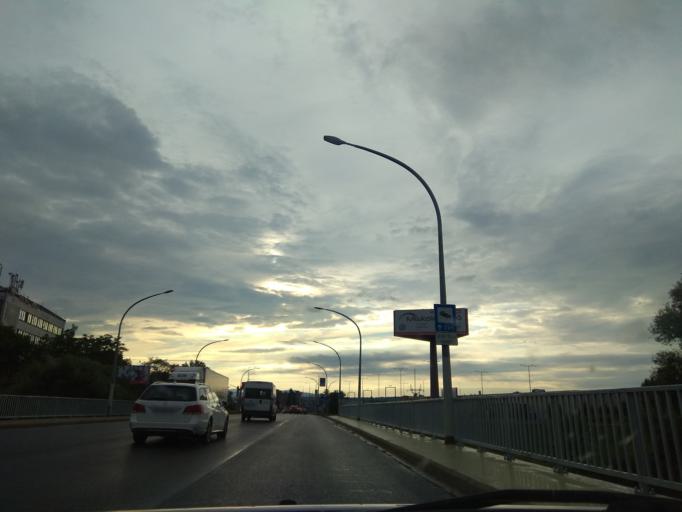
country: HU
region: Borsod-Abauj-Zemplen
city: Miskolc
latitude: 48.1068
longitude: 20.8241
